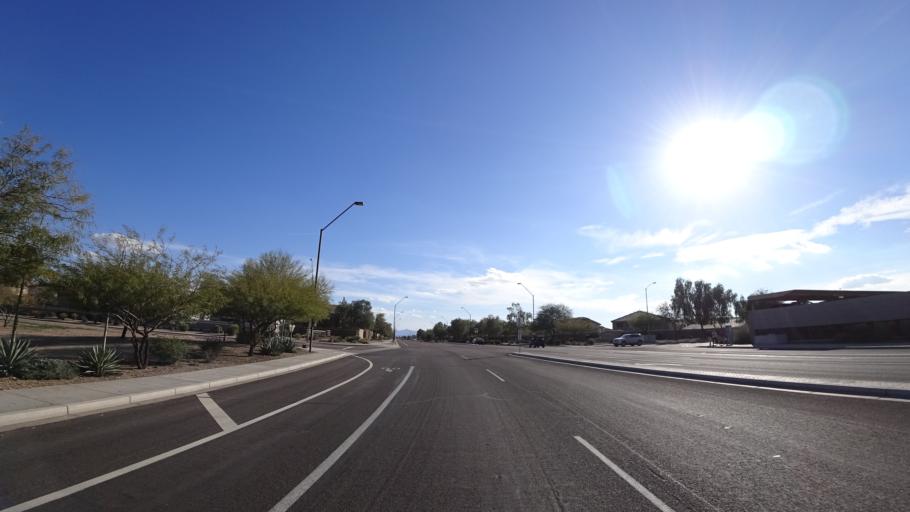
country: US
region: Arizona
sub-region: Maricopa County
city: Peoria
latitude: 33.5741
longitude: -112.2376
